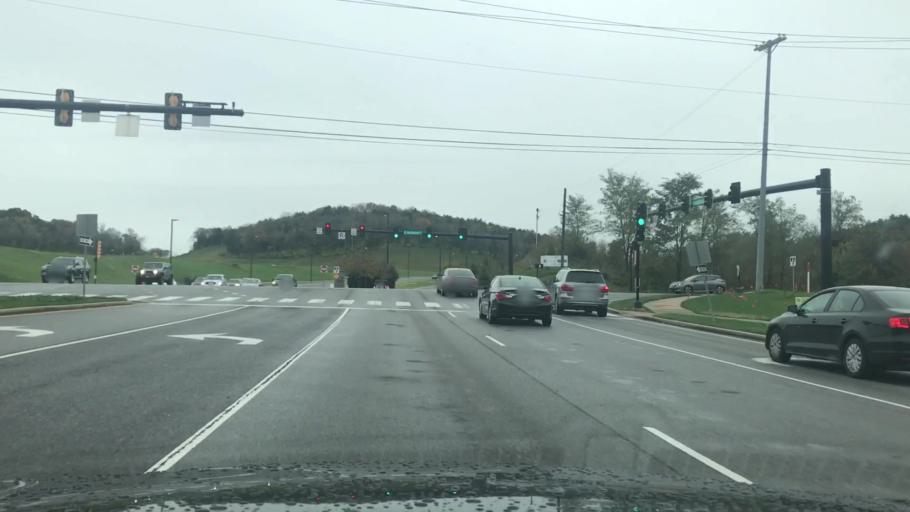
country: US
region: Tennessee
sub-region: Williamson County
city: Franklin
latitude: 35.9335
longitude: -86.8117
